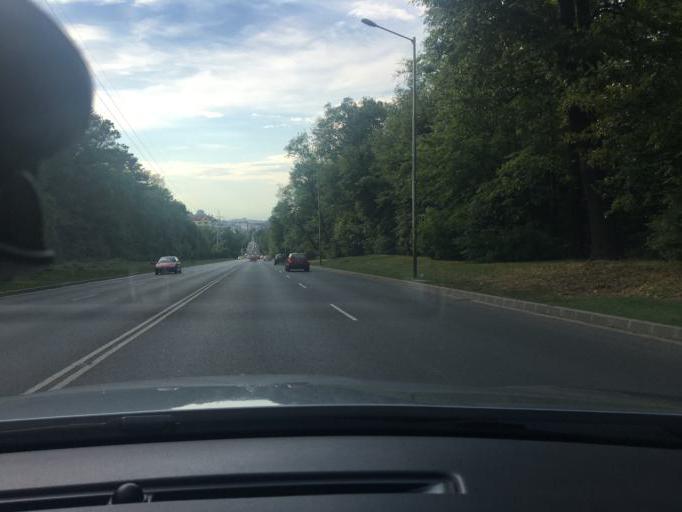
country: BG
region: Sofia-Capital
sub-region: Stolichna Obshtina
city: Sofia
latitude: 42.6792
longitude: 23.3398
